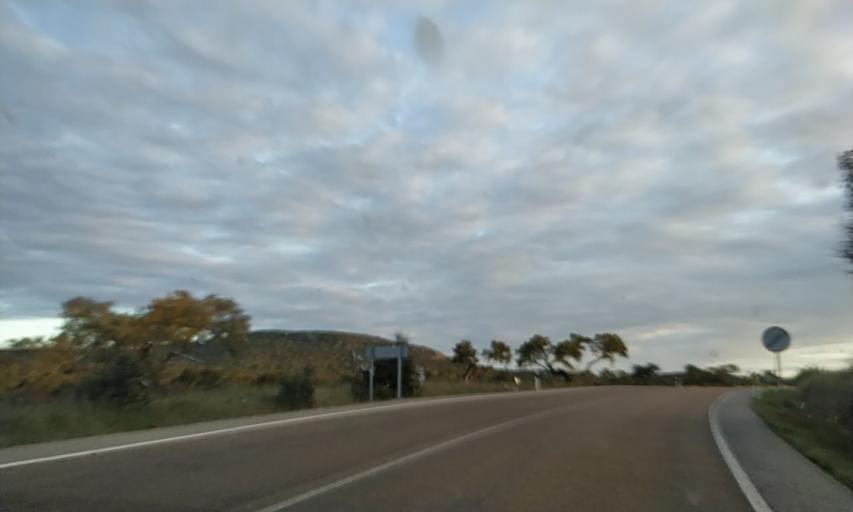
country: ES
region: Extremadura
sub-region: Provincia de Badajoz
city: Puebla de Obando
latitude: 39.2130
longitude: -6.5831
